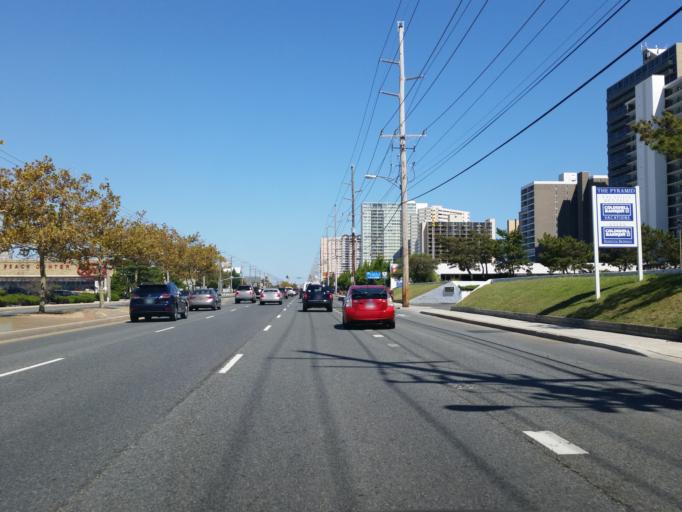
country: US
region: Maryland
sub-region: Worcester County
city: Ocean City
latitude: 38.4102
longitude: -75.0584
